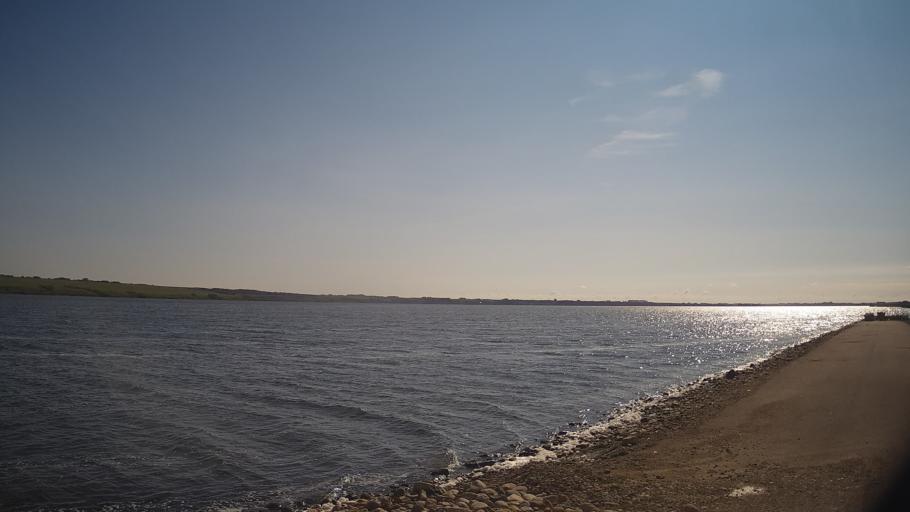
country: CA
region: Saskatchewan
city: Watrous
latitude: 51.7183
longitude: -105.4243
